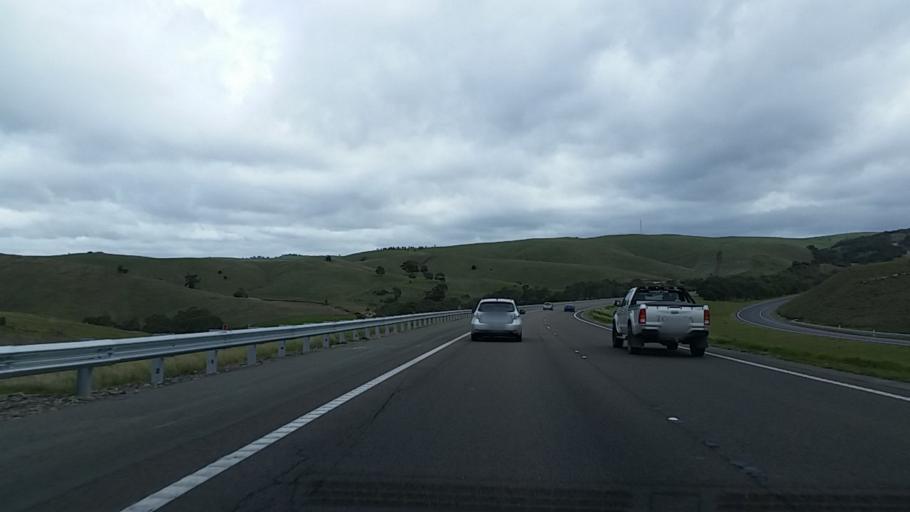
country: AU
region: South Australia
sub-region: Mount Barker
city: Callington
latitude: -35.1156
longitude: 138.9969
